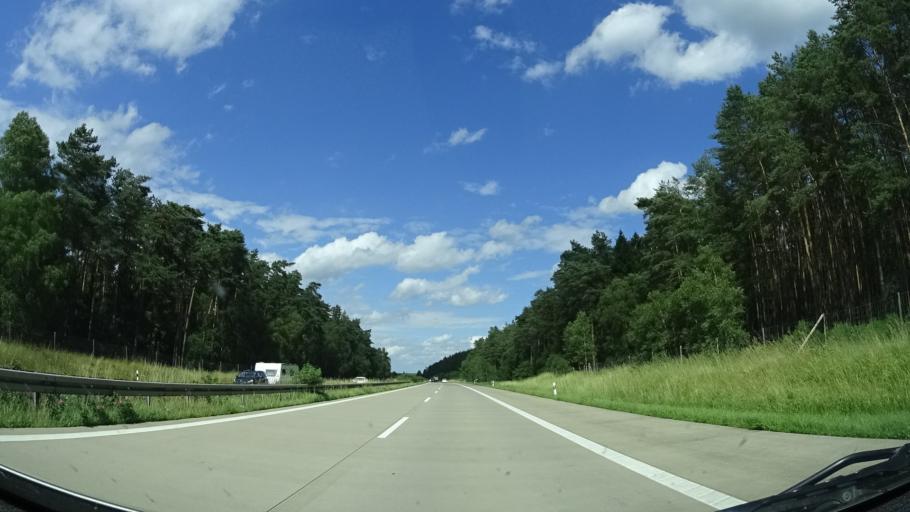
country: DE
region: Mecklenburg-Vorpommern
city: Krakow am See
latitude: 53.5932
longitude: 12.3580
